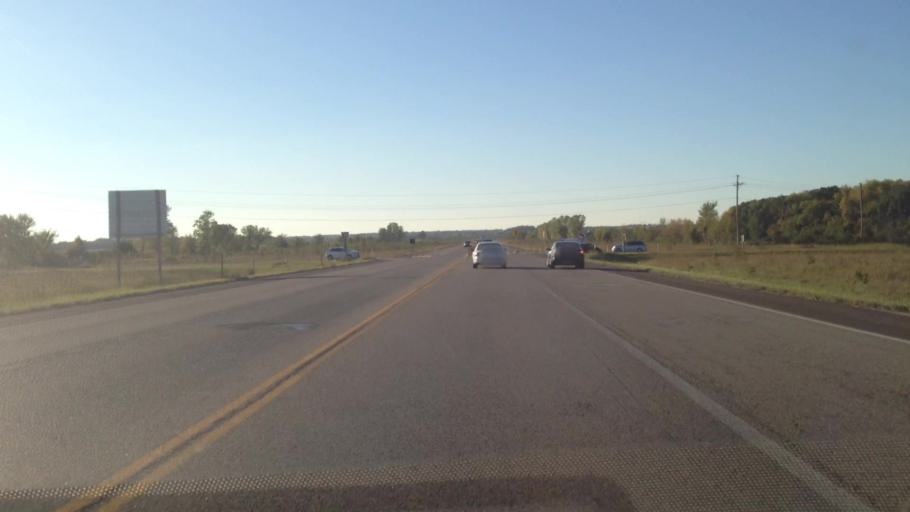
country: US
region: Kansas
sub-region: Douglas County
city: Lawrence
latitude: 38.9228
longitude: -95.2764
